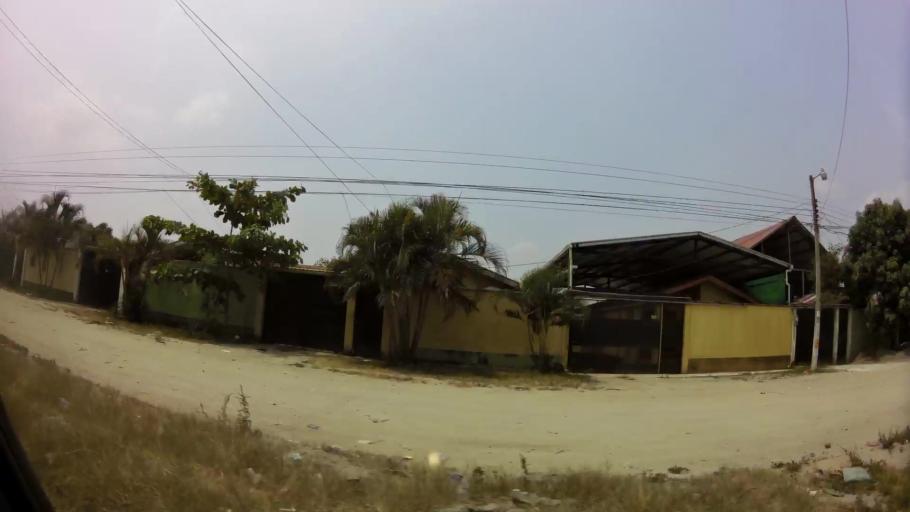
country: HN
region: Cortes
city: San Pedro Sula
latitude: 15.4776
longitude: -87.9889
